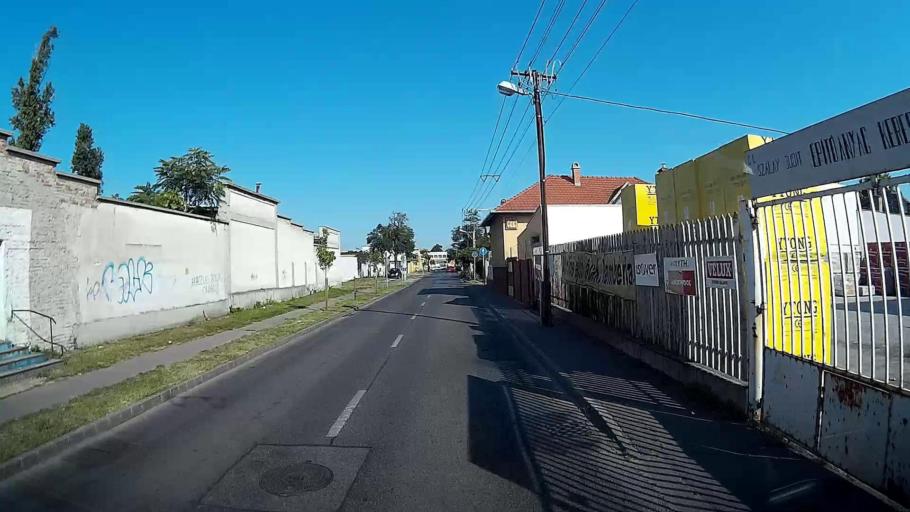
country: HU
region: Budapest
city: Budapest XX. keruelet
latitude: 47.4282
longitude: 19.1070
